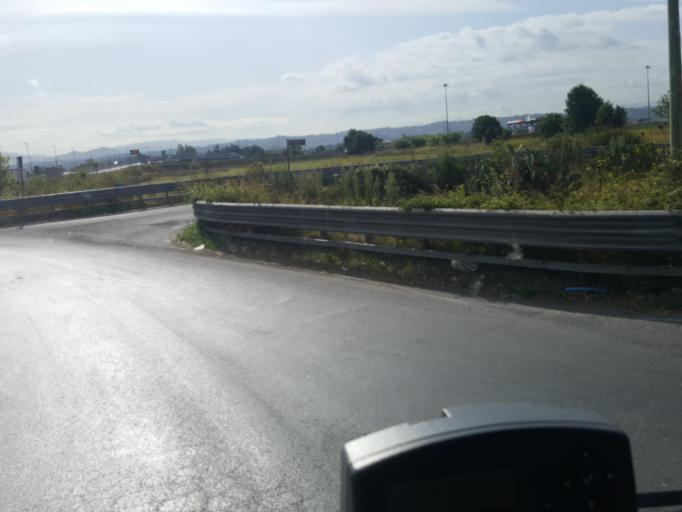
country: IT
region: Latium
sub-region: Citta metropolitana di Roma Capitale
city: Girardi-Bellavista-Terrazze
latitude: 42.0939
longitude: 12.5655
